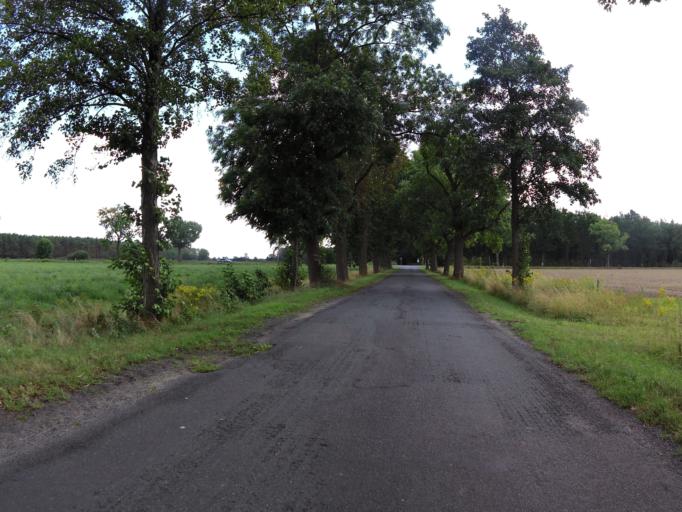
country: DE
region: Brandenburg
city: Storkow
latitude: 52.2333
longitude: 13.8728
